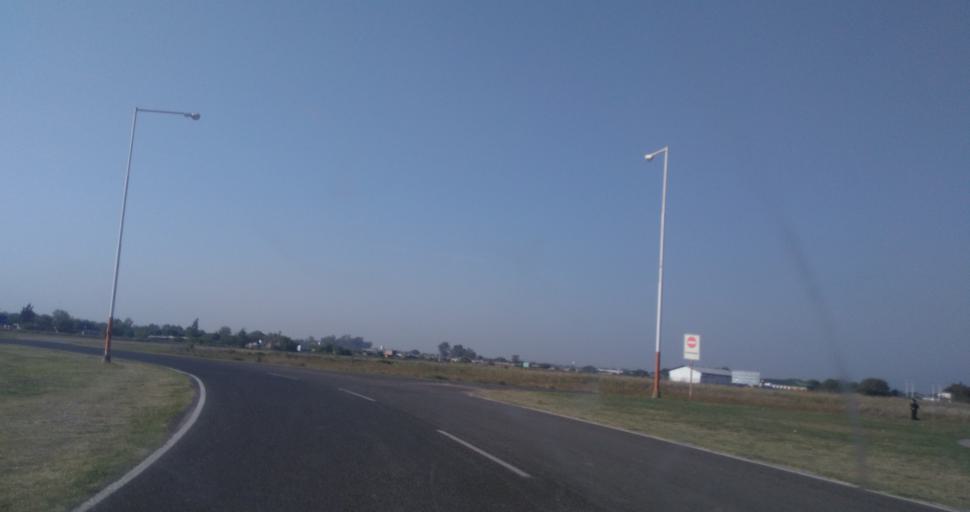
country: AR
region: Chaco
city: Fontana
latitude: -27.4439
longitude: -59.0434
